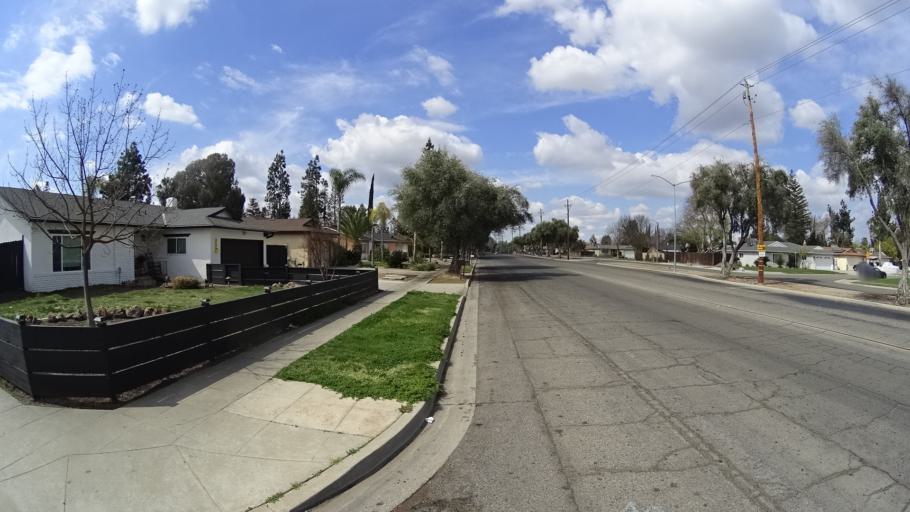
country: US
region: California
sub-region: Fresno County
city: Fresno
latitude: 36.8227
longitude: -119.8547
